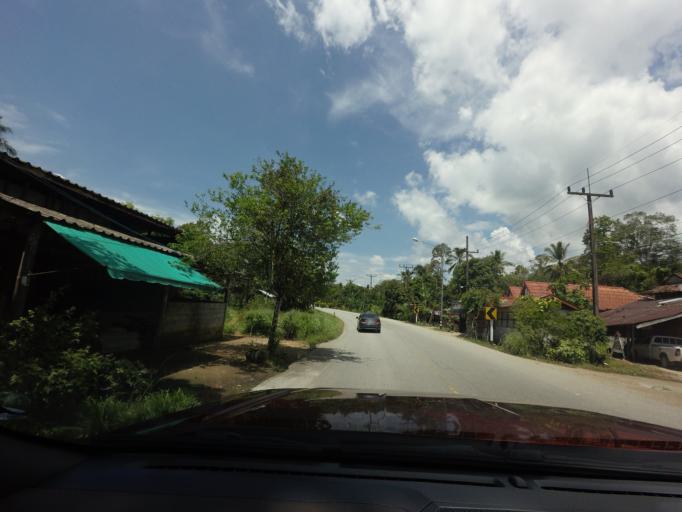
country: TH
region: Narathiwat
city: Chanae
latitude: 6.1984
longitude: 101.6867
